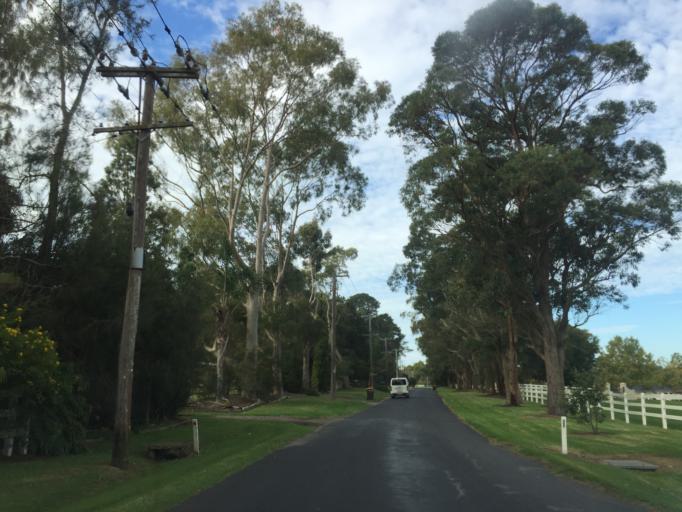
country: AU
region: New South Wales
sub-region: Hornsby Shire
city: Galston
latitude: -33.6479
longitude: 151.0697
